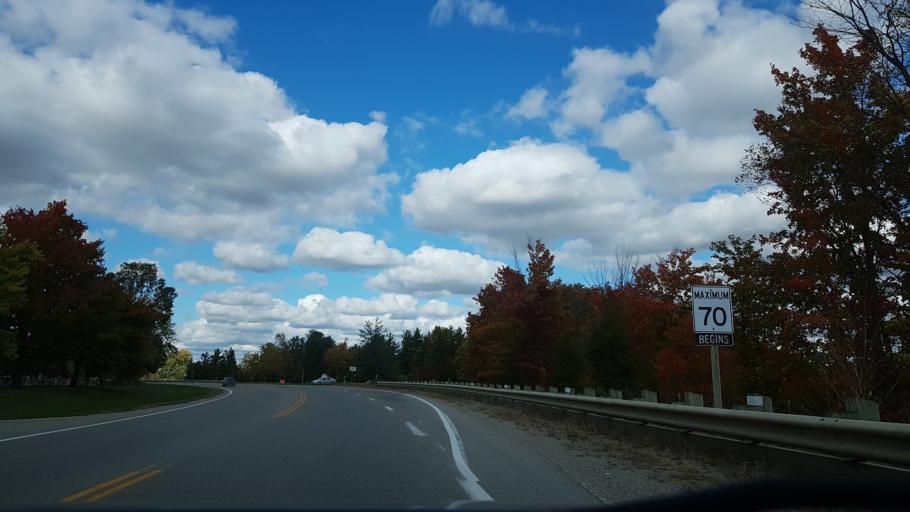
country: CA
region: Ontario
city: South Huron
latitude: 43.1705
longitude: -81.6795
